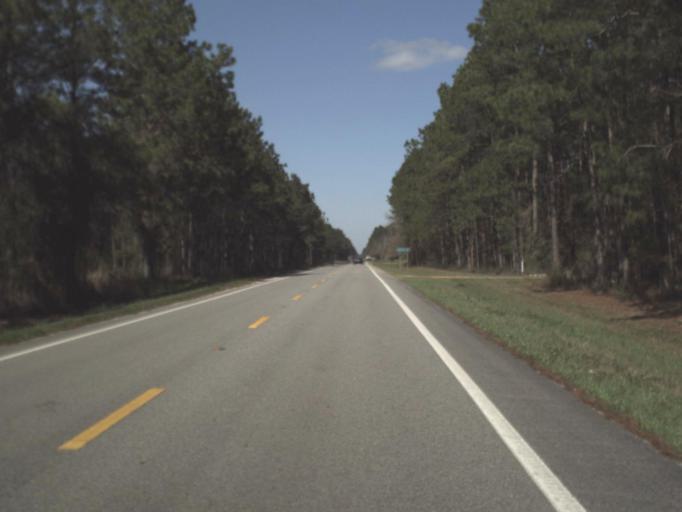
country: US
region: Florida
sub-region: Gulf County
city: Port Saint Joe
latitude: 29.9339
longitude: -85.1914
